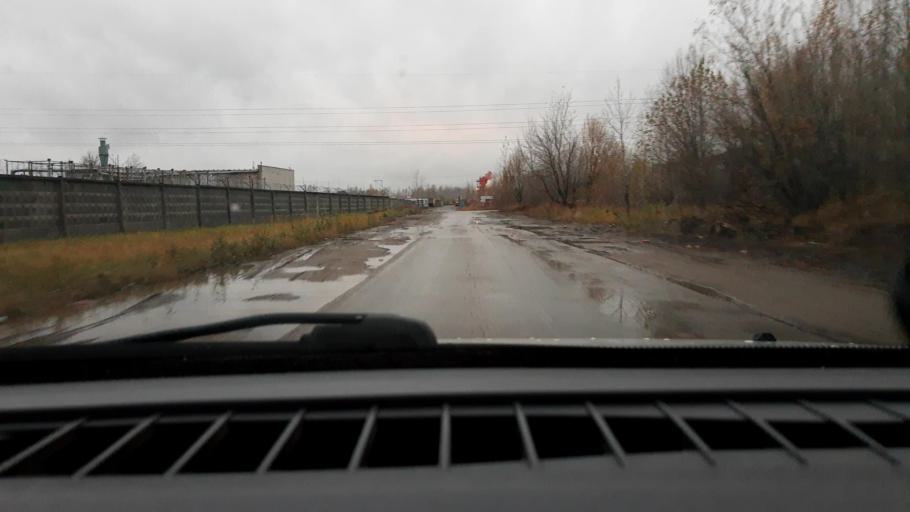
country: RU
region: Nizjnij Novgorod
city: Gorbatovka
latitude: 56.2716
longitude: 43.8520
